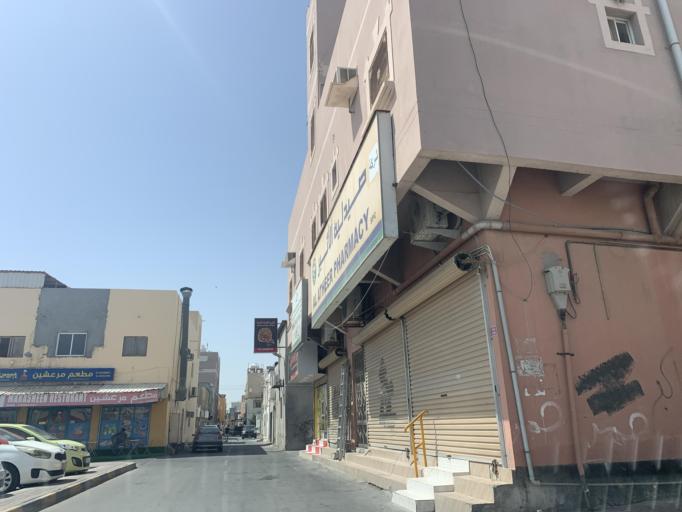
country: BH
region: Northern
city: Sitrah
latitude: 26.1601
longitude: 50.6159
